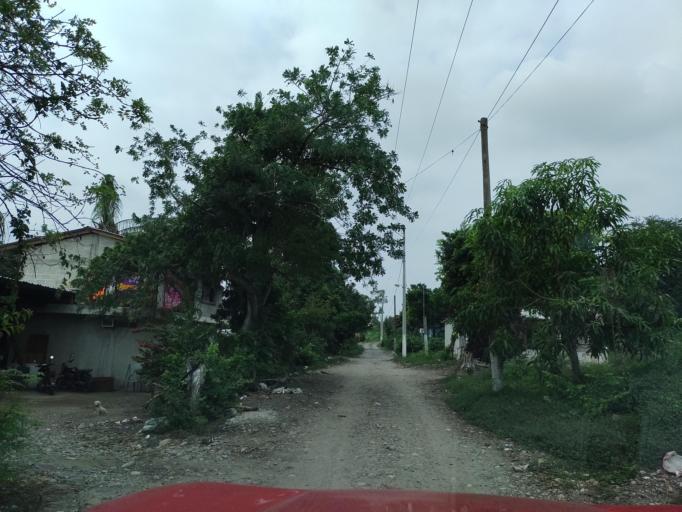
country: MX
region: Veracruz
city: Agua Dulce
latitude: 20.3413
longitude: -97.2934
